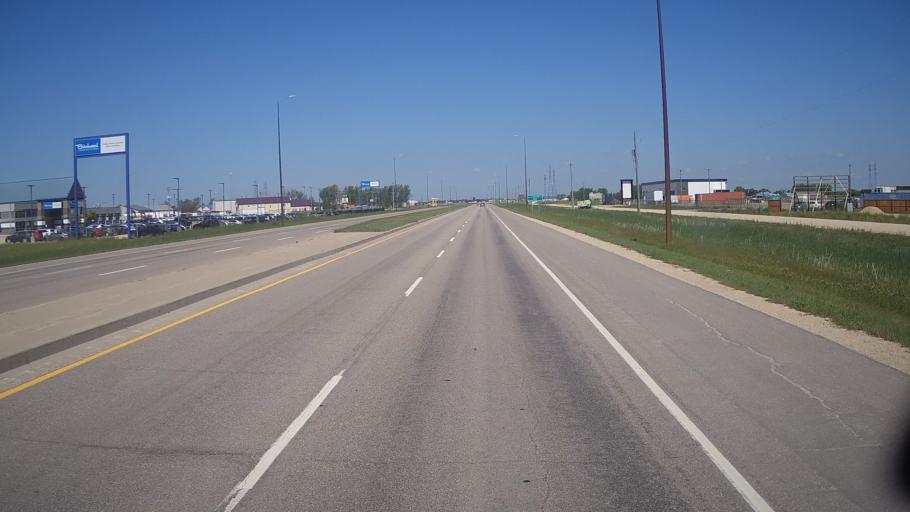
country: CA
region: Manitoba
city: Winnipeg
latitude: 49.8457
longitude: -96.9945
